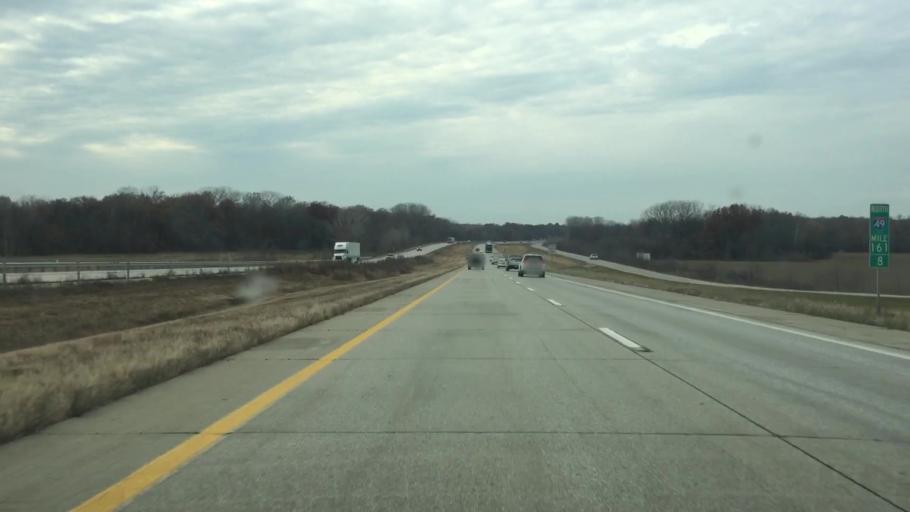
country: US
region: Missouri
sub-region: Cass County
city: Harrisonville
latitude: 38.6638
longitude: -94.3909
